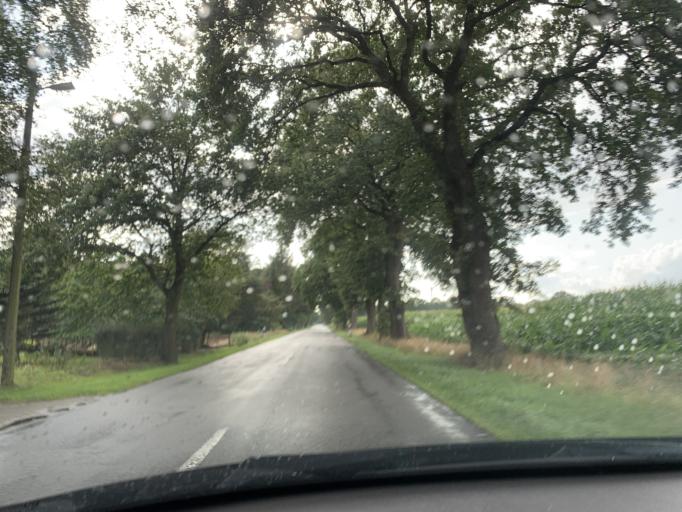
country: DE
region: Lower Saxony
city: Zetel
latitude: 53.3503
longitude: 7.9579
